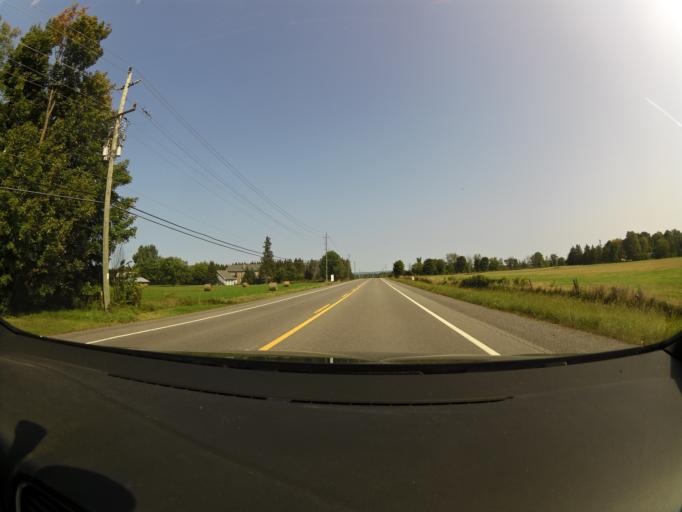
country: CA
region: Ontario
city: Arnprior
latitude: 45.4167
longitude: -76.2678
